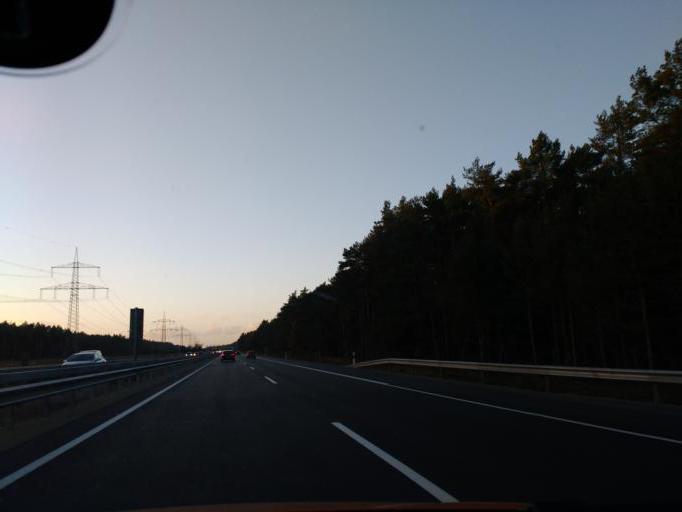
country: DE
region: Schleswig-Holstein
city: Gudow
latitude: 53.5229
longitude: 10.7964
